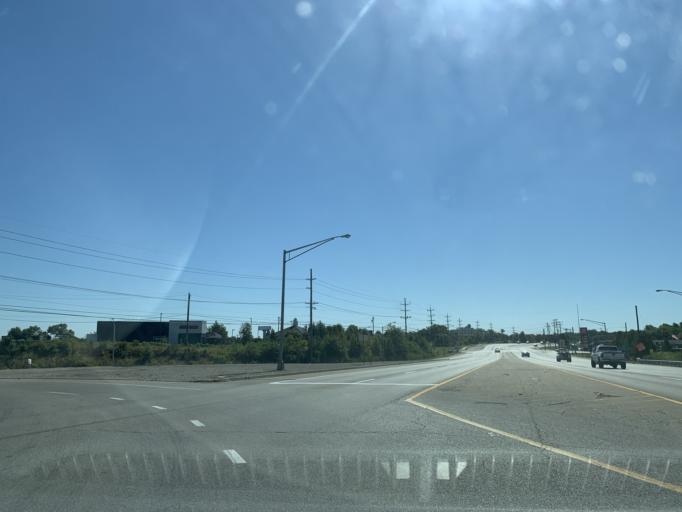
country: US
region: Kentucky
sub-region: Boone County
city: Hebron
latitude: 39.0800
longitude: -84.7083
